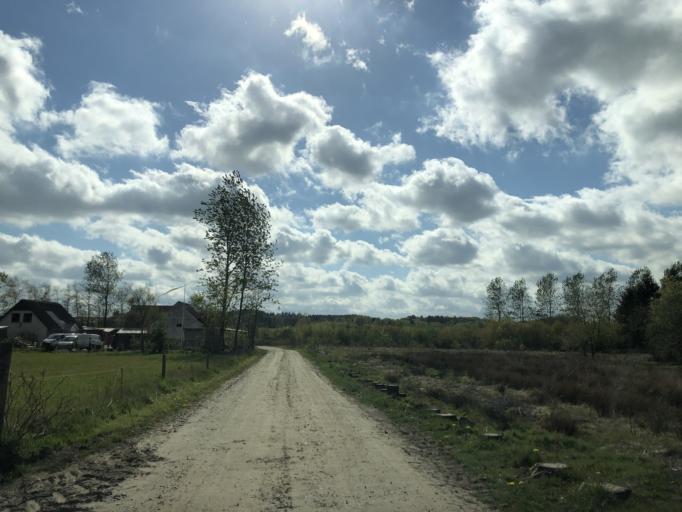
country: DK
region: Central Jutland
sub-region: Herning Kommune
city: Avlum
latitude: 56.2992
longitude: 8.7622
